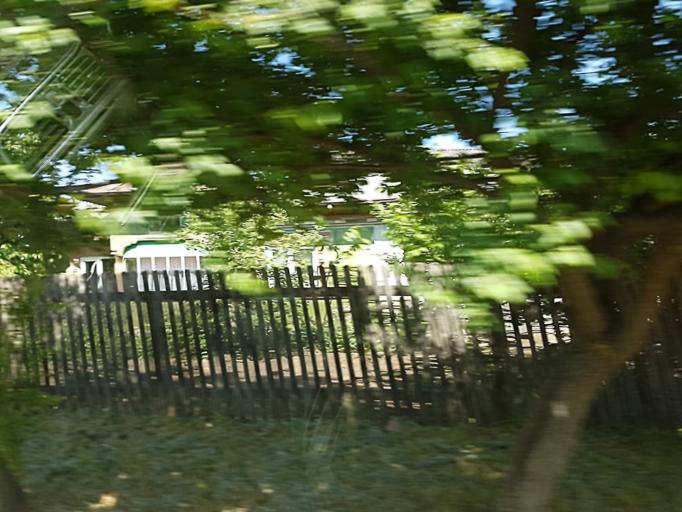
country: RO
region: Giurgiu
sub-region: Comuna Herasti
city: Herasti
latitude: 44.2150
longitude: 26.3590
